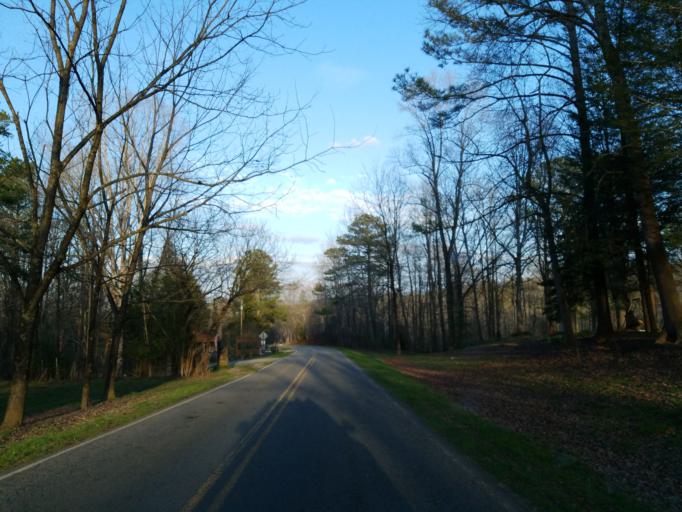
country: US
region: Georgia
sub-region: Pickens County
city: Jasper
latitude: 34.5056
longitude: -84.5208
